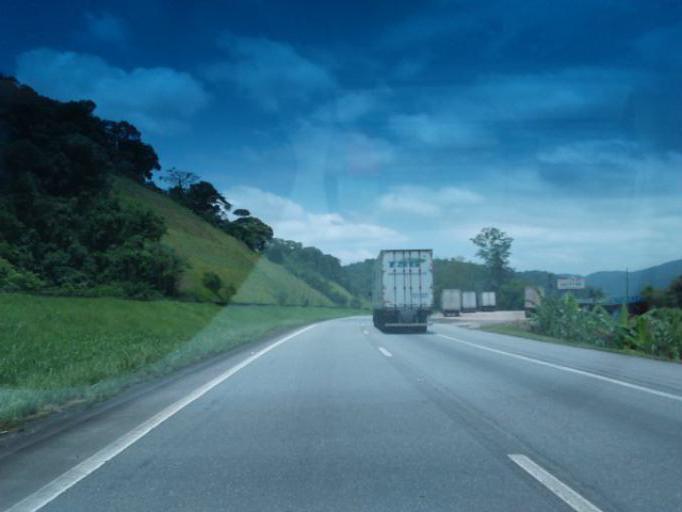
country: BR
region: Sao Paulo
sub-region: Miracatu
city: Miracatu
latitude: -24.1810
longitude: -47.3525
